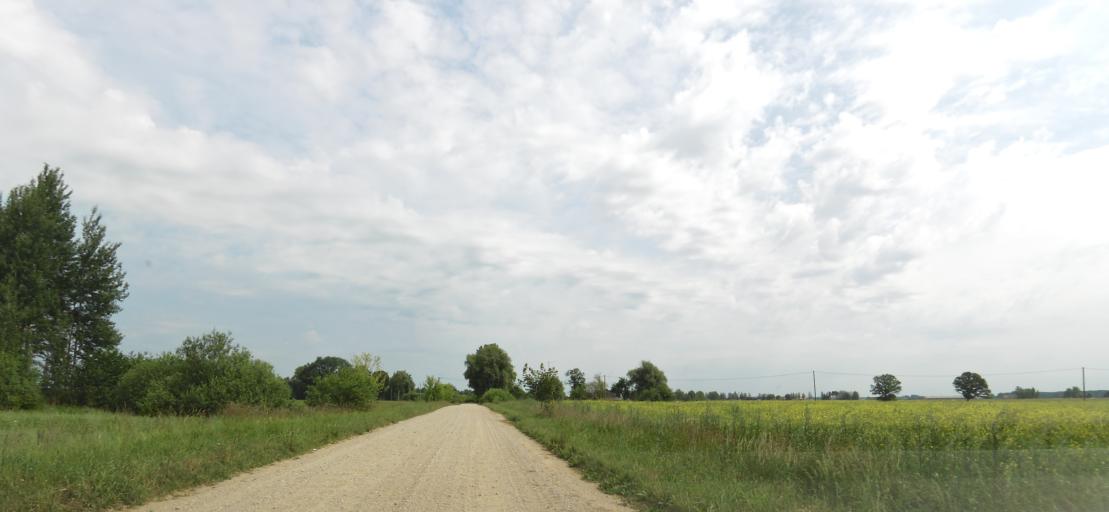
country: LT
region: Panevezys
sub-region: Birzai
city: Birzai
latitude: 56.3230
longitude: 24.6982
